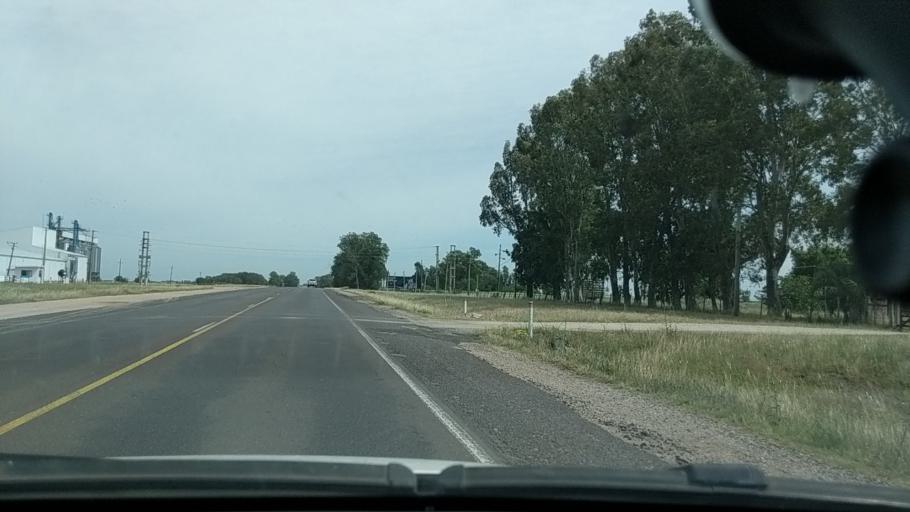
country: UY
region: Durazno
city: Durazno
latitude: -33.4962
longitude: -56.4276
